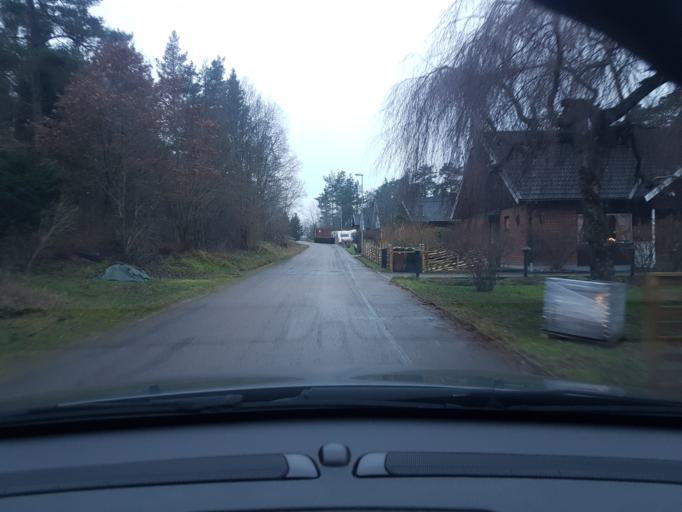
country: SE
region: Vaestra Goetaland
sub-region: Ale Kommun
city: Alvangen
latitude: 57.9532
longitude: 12.1346
